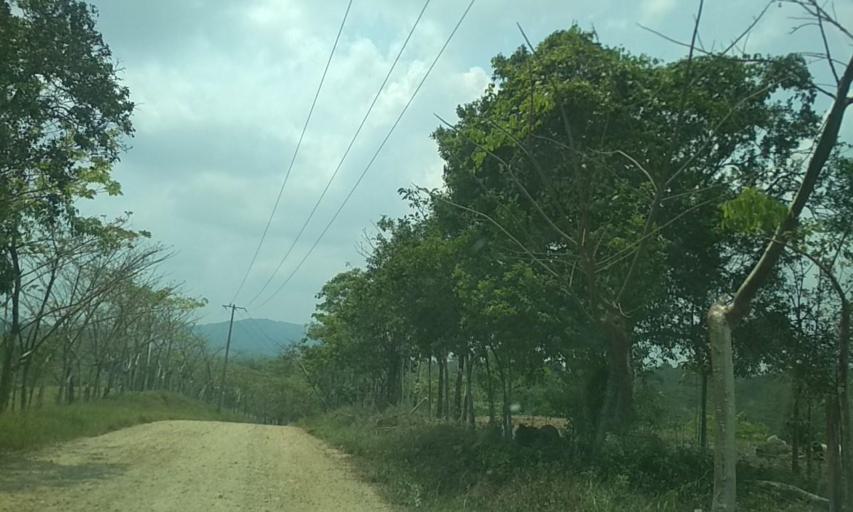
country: MX
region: Tabasco
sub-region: Huimanguillo
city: Francisco Rueda
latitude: 17.6078
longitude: -93.8075
